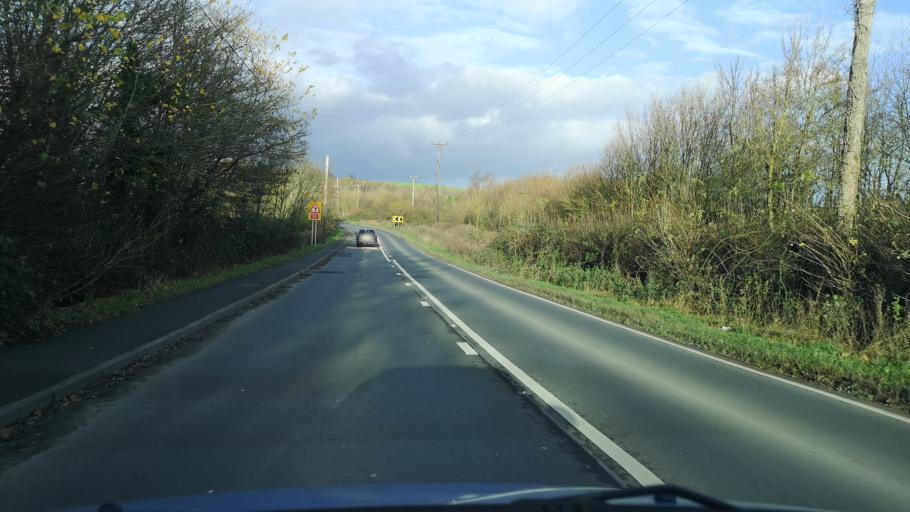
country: GB
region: England
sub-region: City and Borough of Wakefield
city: Featherstone
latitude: 53.6856
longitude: -1.3758
